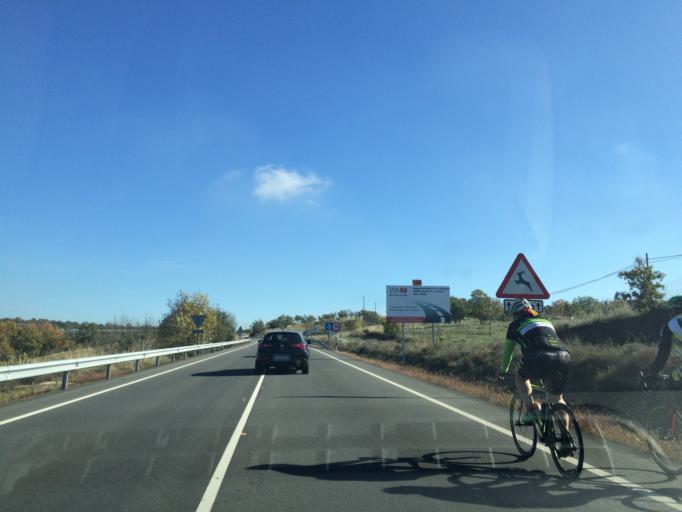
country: ES
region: Madrid
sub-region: Provincia de Madrid
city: Miraflores de la Sierra
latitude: 40.7597
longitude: -3.7631
